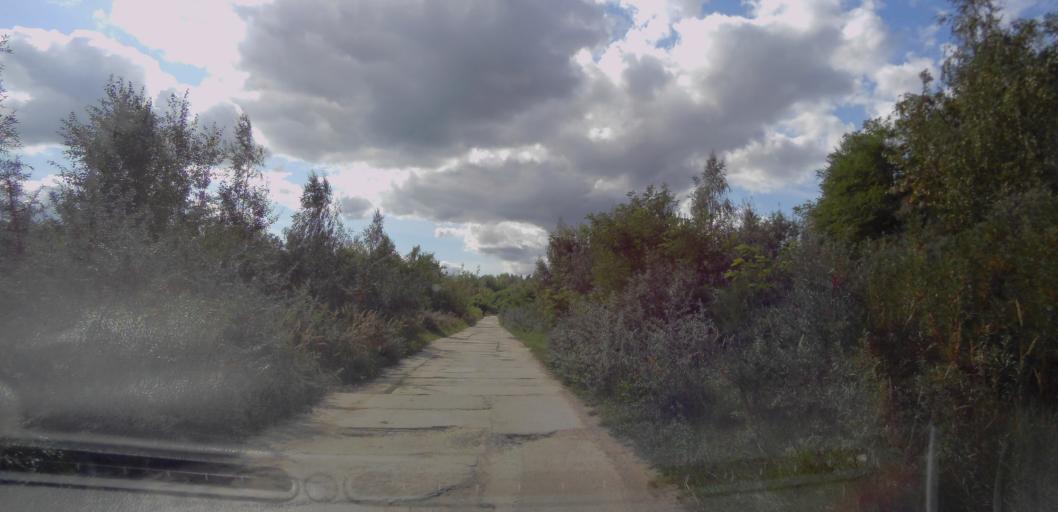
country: PL
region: Subcarpathian Voivodeship
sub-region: Tarnobrzeg
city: Tarnobrzeg
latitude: 50.5344
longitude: 21.6639
